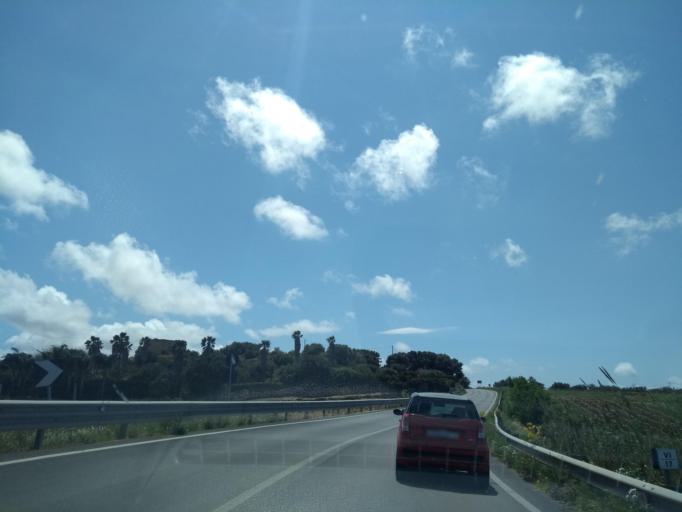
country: IT
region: Sicily
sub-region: Trapani
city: Marsala
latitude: 37.8753
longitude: 12.5215
